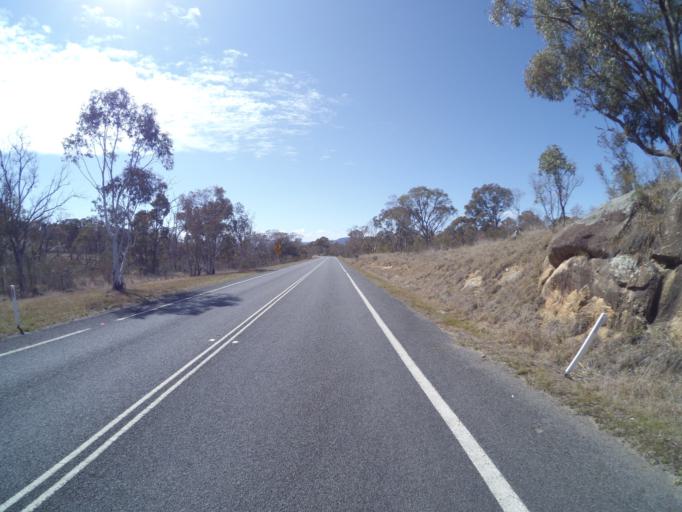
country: AU
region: Australian Capital Territory
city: Macarthur
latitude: -35.4618
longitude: 149.0319
